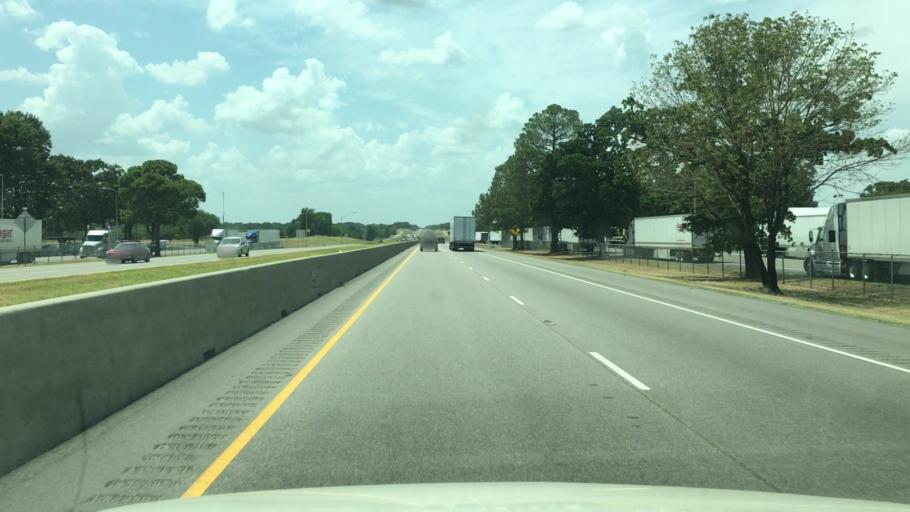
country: US
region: Texas
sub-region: Franklin County
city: Mount Vernon
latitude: 33.1650
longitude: -95.2852
